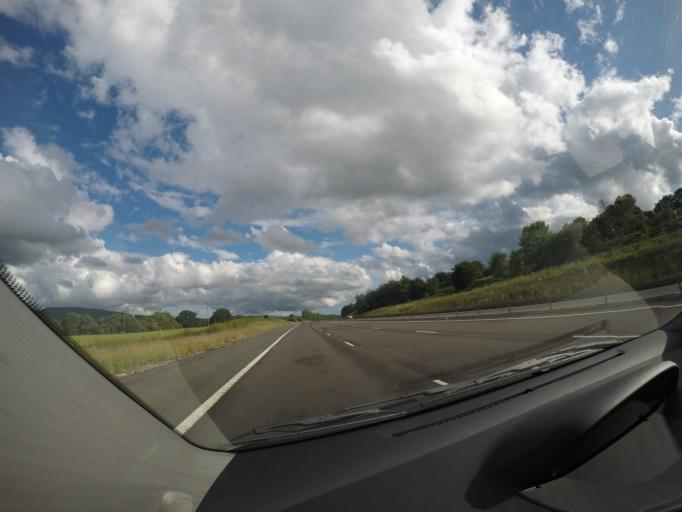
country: GB
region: Scotland
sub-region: Dumfries and Galloway
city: Moffat
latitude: 55.2558
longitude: -3.4119
